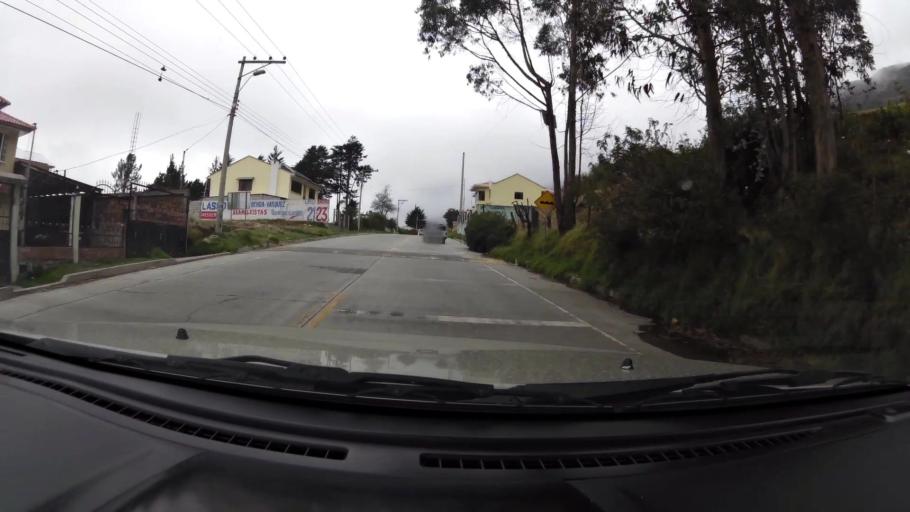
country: EC
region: Canar
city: Canar
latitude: -2.4806
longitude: -78.9815
